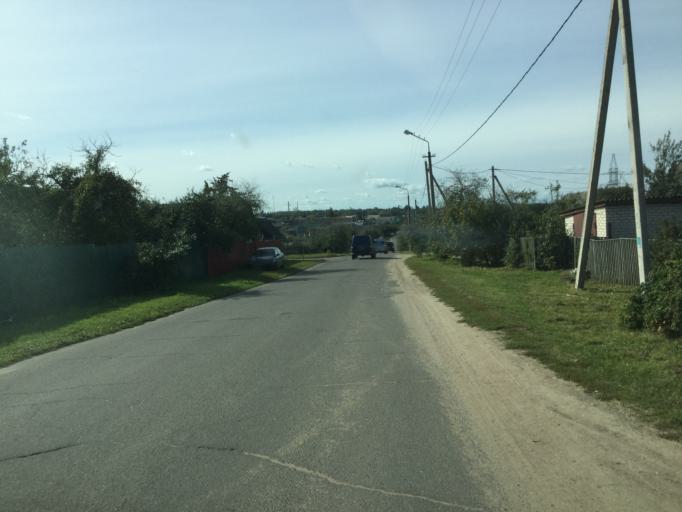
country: BY
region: Vitebsk
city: Orsha
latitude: 54.5478
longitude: 30.4413
